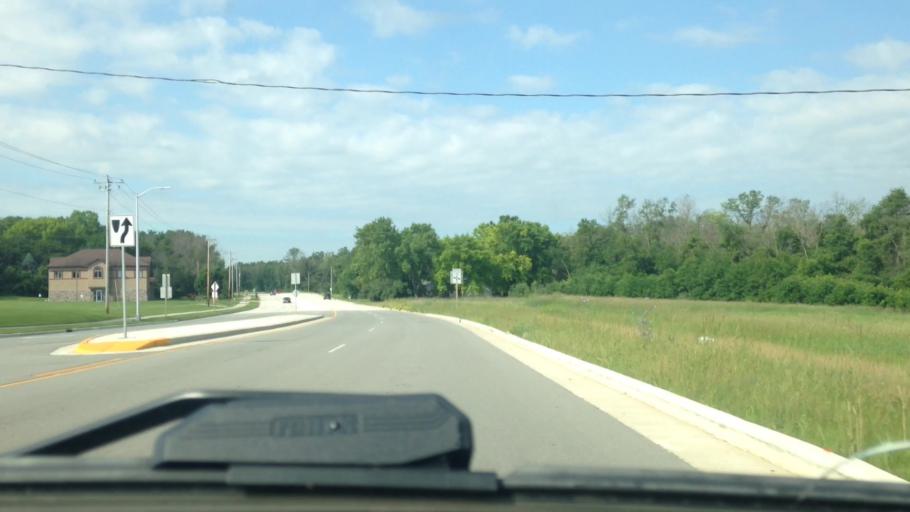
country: US
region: Wisconsin
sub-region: Waukesha County
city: Menomonee Falls
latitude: 43.2054
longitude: -88.1584
